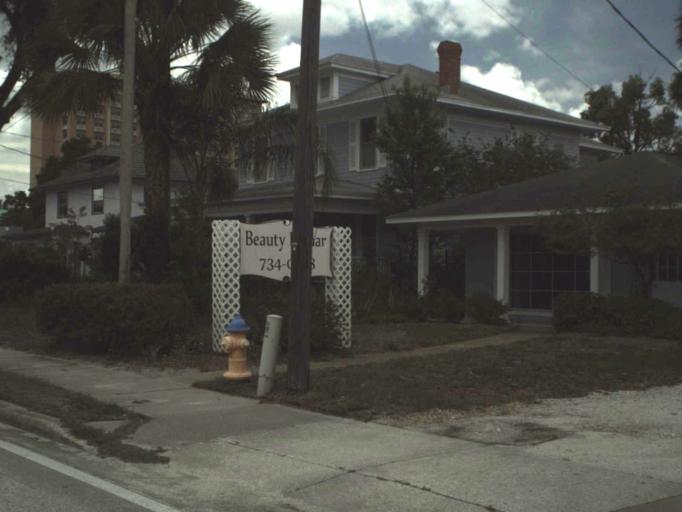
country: US
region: Florida
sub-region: Volusia County
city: DeLand
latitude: 29.0281
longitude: -81.2971
